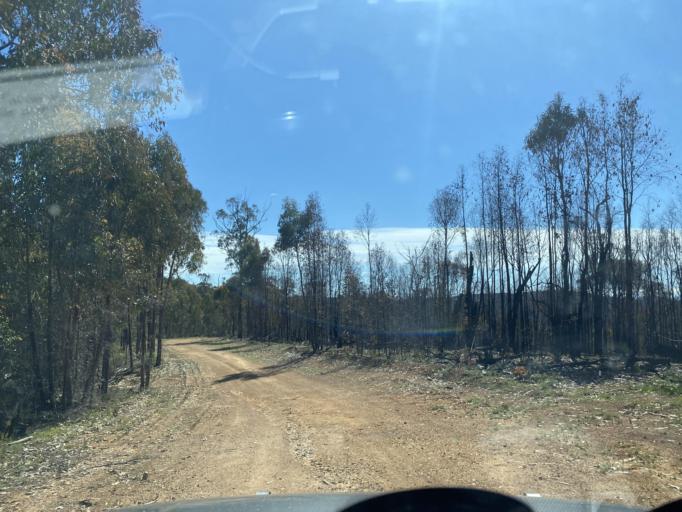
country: AU
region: Victoria
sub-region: Benalla
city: Benalla
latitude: -36.7377
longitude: 146.1814
